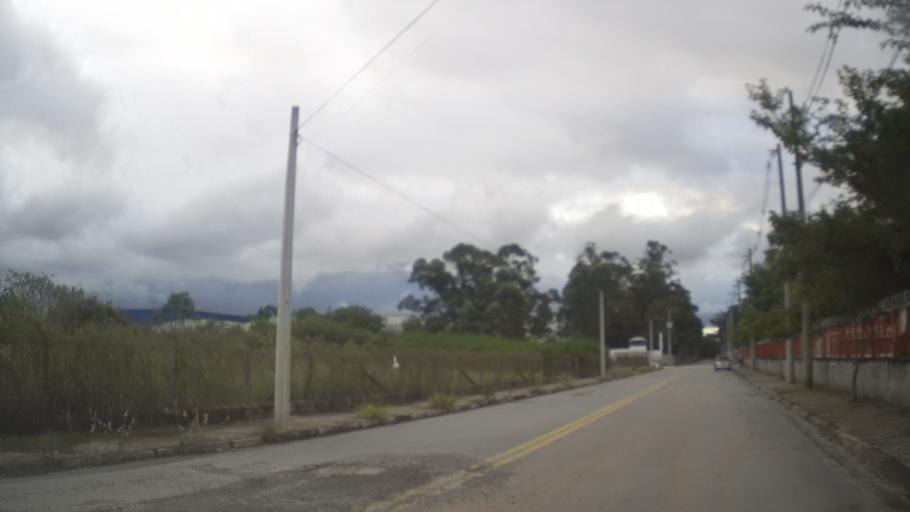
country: BR
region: Sao Paulo
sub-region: Guarulhos
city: Guarulhos
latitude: -23.4746
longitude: -46.4518
